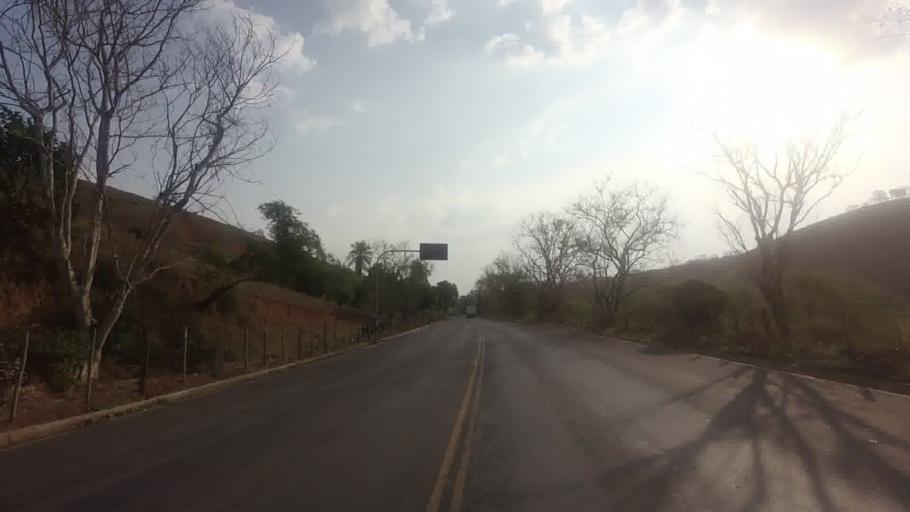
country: BR
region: Rio de Janeiro
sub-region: Itaperuna
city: Itaperuna
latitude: -21.3704
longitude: -41.9441
